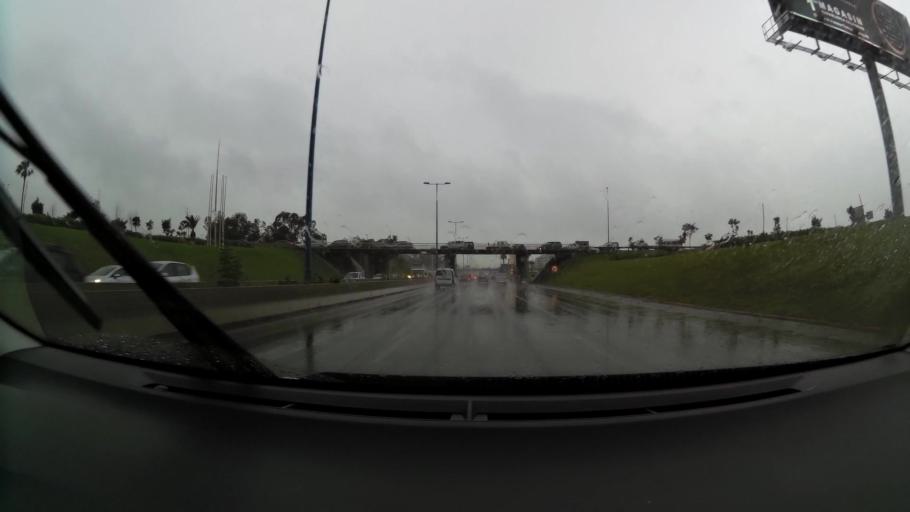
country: MA
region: Grand Casablanca
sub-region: Casablanca
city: Casablanca
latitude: 33.5679
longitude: -7.5748
